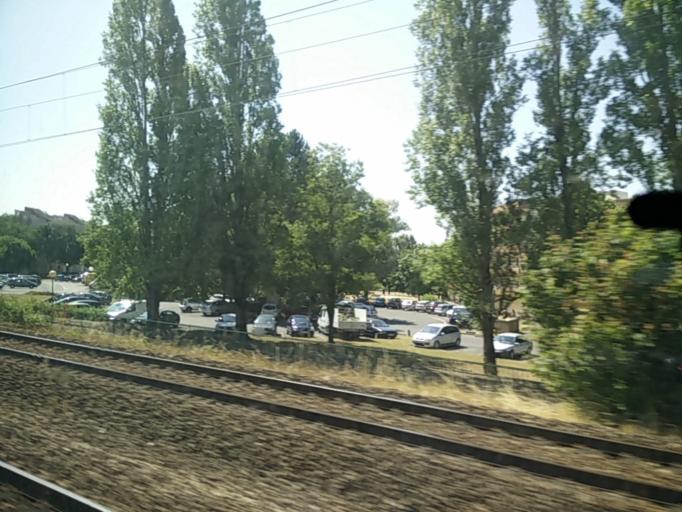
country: FR
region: Ile-de-France
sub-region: Departement de Seine-et-Marne
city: Roissy-en-Brie
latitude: 48.7986
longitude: 2.6418
